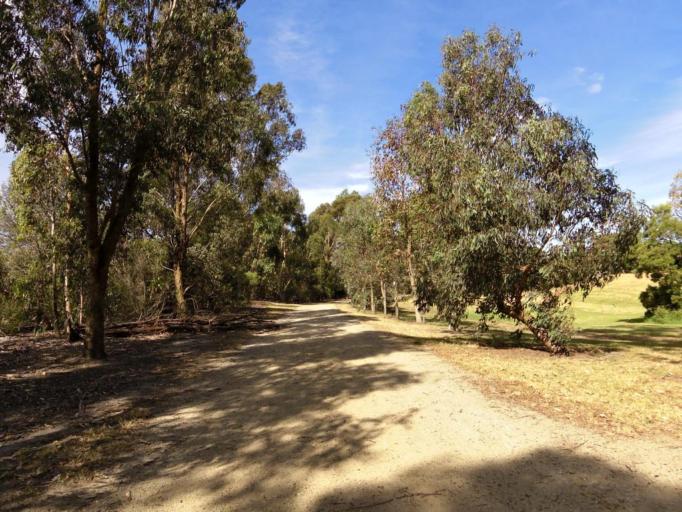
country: AU
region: Victoria
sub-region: Casey
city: Doveton
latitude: -37.9998
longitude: 145.2402
